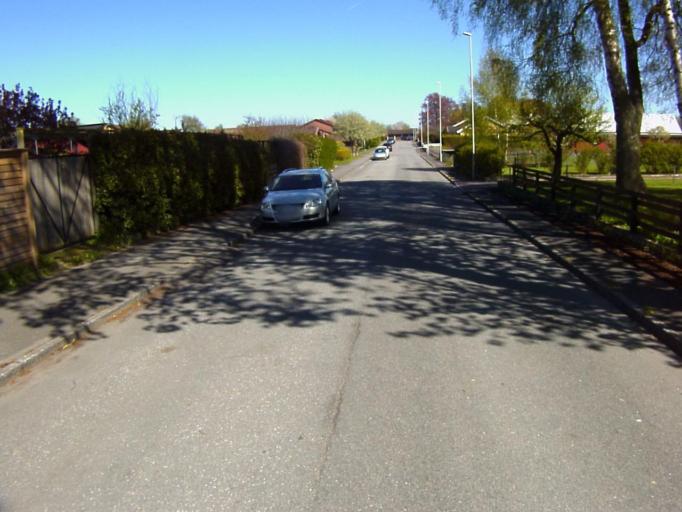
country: SE
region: Skane
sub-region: Kristianstads Kommun
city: Kristianstad
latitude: 56.0293
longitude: 14.1999
